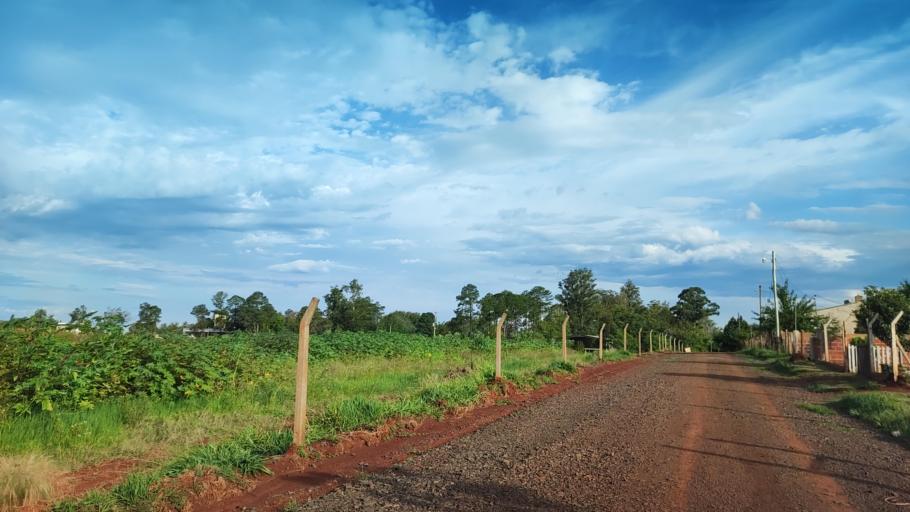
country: AR
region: Misiones
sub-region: Departamento de Capital
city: Posadas
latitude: -27.4453
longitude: -55.9604
